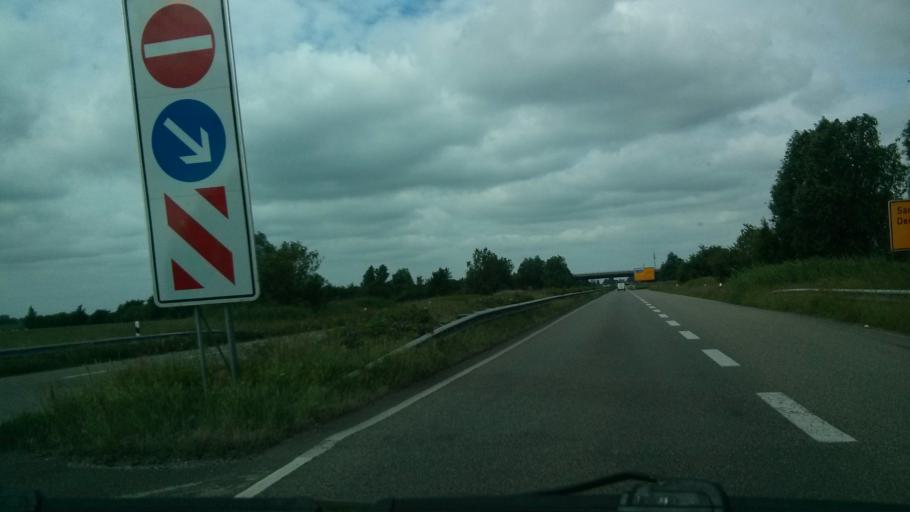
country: DE
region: Lower Saxony
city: Nordenham
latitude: 53.4377
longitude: 8.5226
